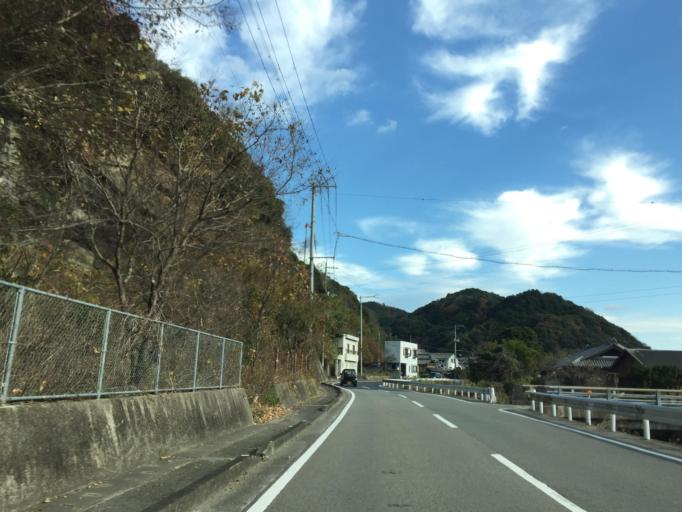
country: JP
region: Wakayama
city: Kainan
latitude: 34.1632
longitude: 135.2551
